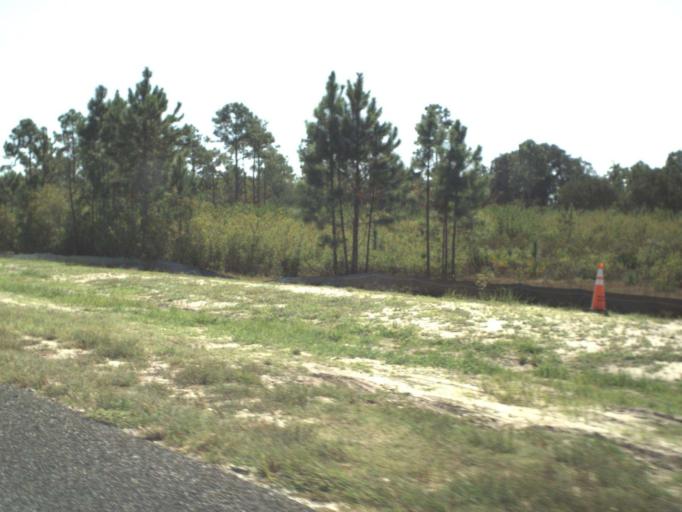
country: US
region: Florida
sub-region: Walton County
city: Seaside
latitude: 30.3540
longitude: -86.0906
